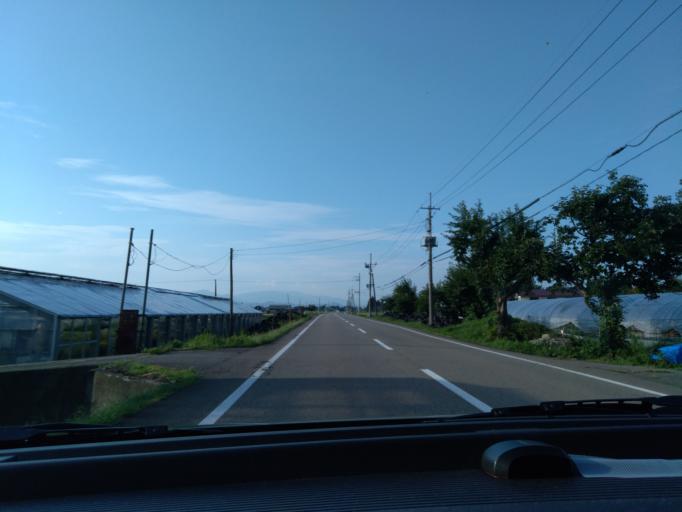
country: JP
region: Akita
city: Kakunodatemachi
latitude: 39.5110
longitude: 140.5590
